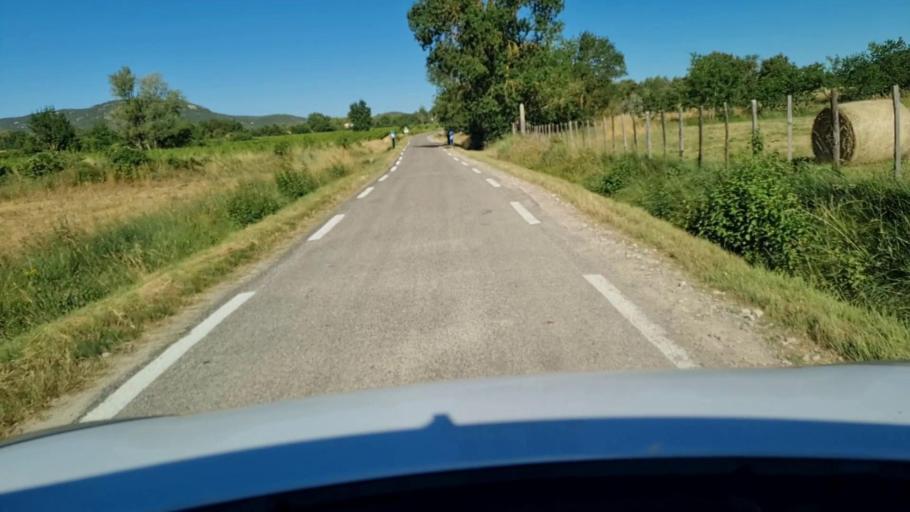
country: FR
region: Languedoc-Roussillon
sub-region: Departement du Gard
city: Sommieres
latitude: 43.8322
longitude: 4.0488
